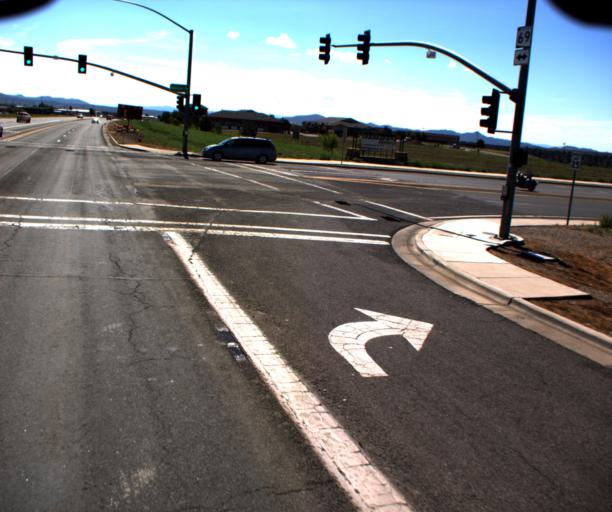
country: US
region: Arizona
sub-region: Yavapai County
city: Prescott Valley
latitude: 34.5856
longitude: -112.3183
